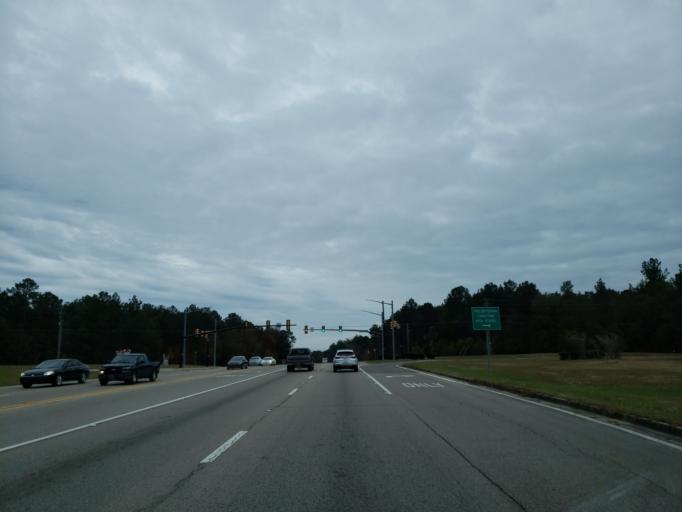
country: US
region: Mississippi
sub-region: Forrest County
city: Hattiesburg
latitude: 31.2930
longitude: -89.3042
